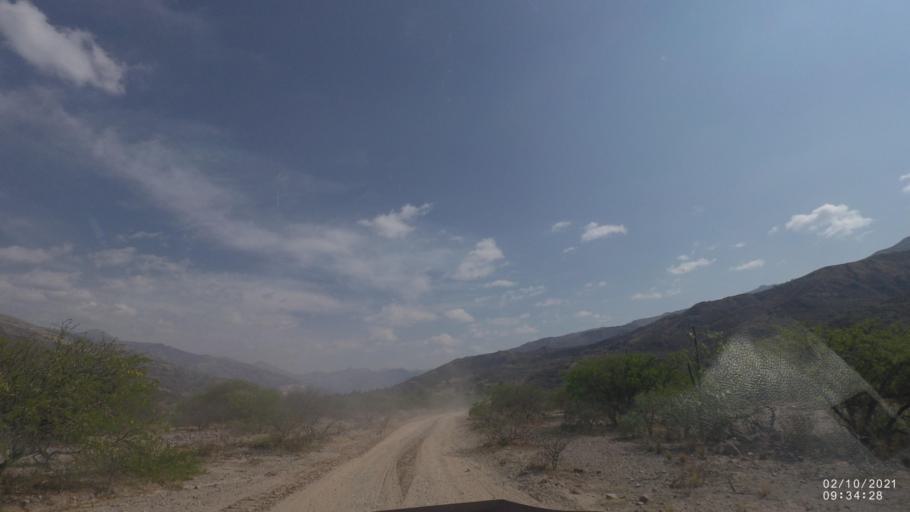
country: BO
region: Cochabamba
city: Irpa Irpa
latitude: -17.8393
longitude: -66.3193
